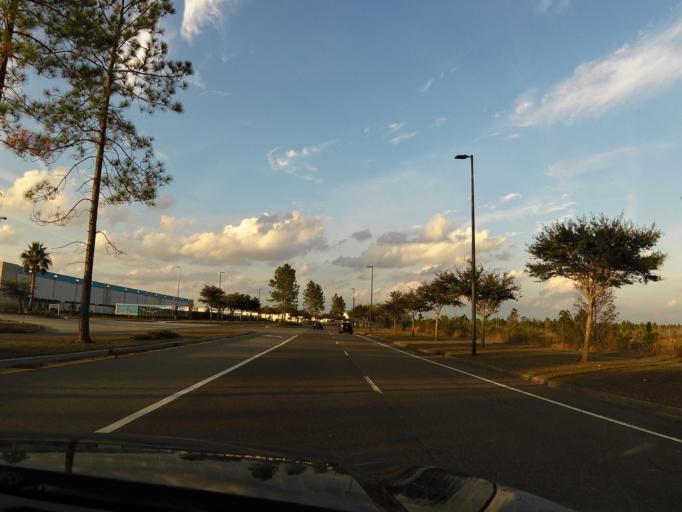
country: US
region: Florida
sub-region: Duval County
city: Baldwin
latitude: 30.2674
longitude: -81.8866
